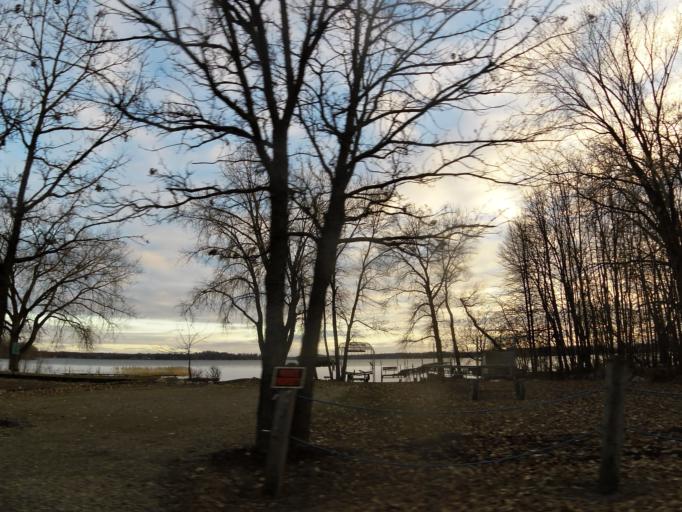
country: US
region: Minnesota
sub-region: Washington County
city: Dellwood
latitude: 45.0980
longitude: -92.9905
